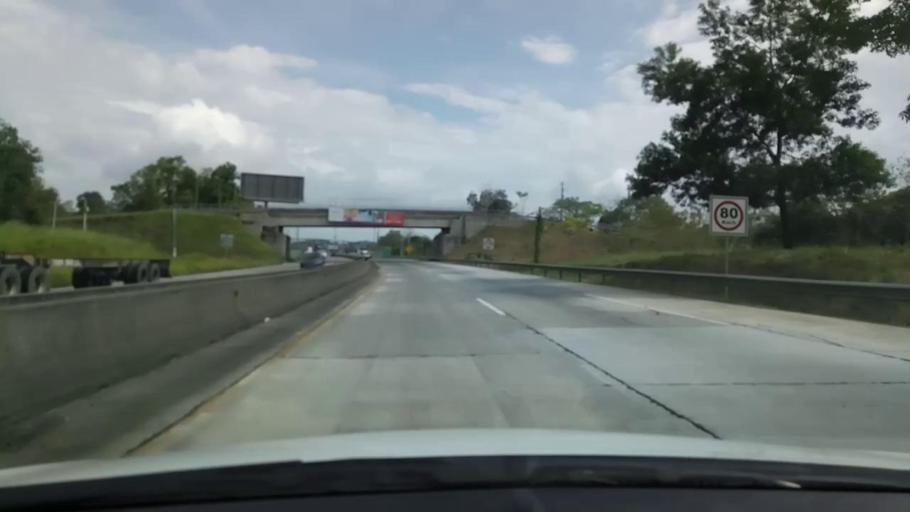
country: PA
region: Colon
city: Buena Vista
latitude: 9.2655
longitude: -79.7042
